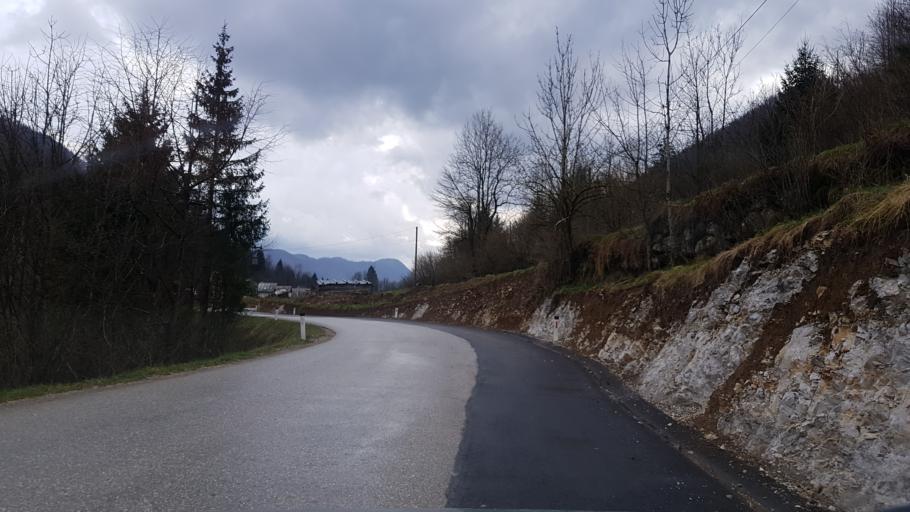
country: SI
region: Tolmin
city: Tolmin
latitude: 46.0915
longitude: 13.7974
